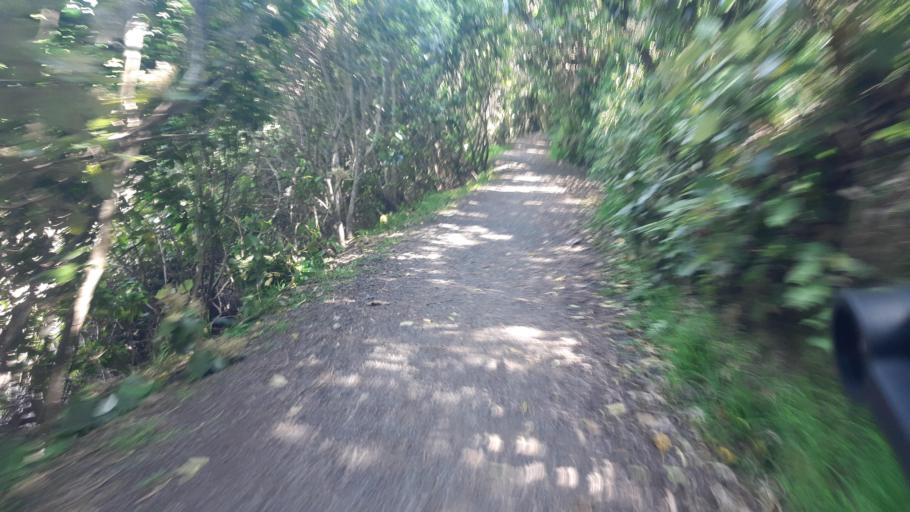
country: NZ
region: Marlborough
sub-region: Marlborough District
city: Picton
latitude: -41.2693
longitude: 174.0331
